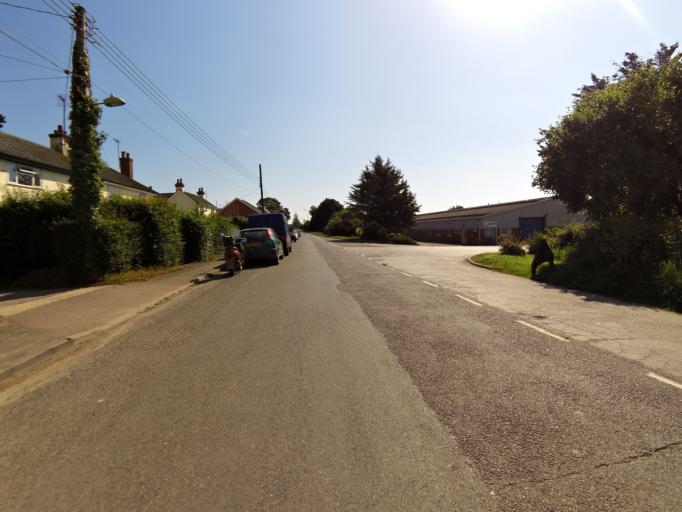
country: GB
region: England
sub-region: Suffolk
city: Bramford
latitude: 52.1071
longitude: 1.0983
